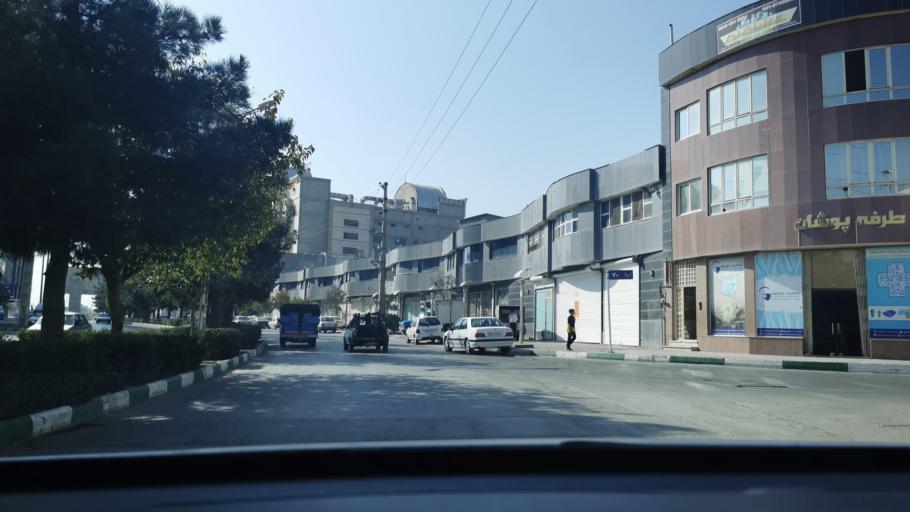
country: IR
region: Razavi Khorasan
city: Mashhad
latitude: 36.3487
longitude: 59.5962
